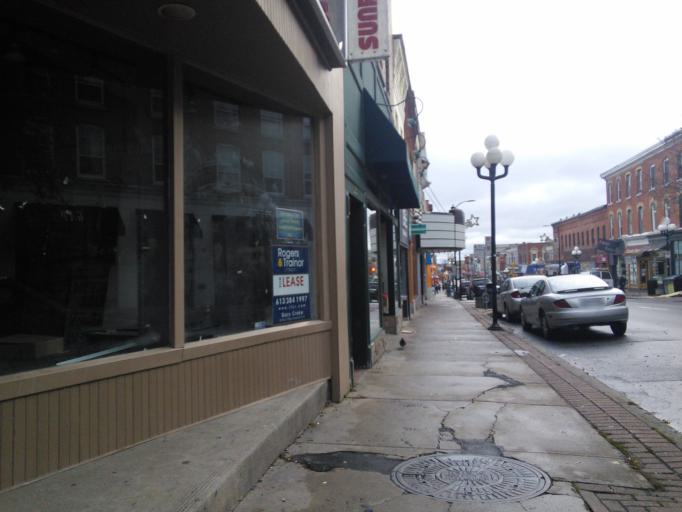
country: CA
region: Ontario
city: Kingston
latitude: 44.2323
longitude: -76.4869
